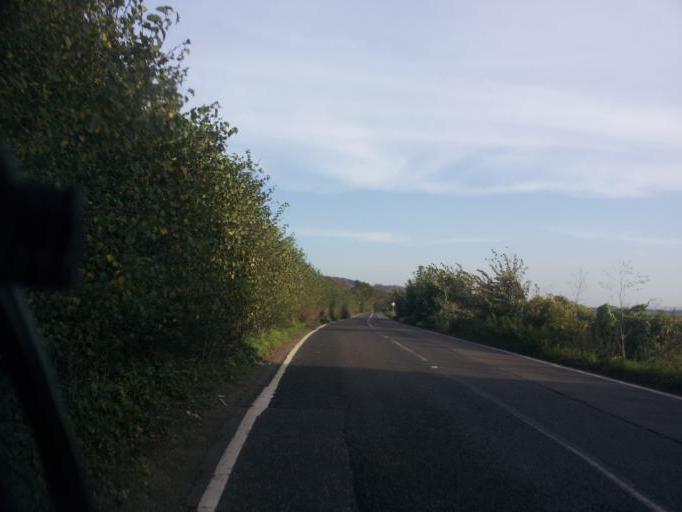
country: GB
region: England
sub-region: Kent
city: Boxley
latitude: 51.3081
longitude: 0.5387
